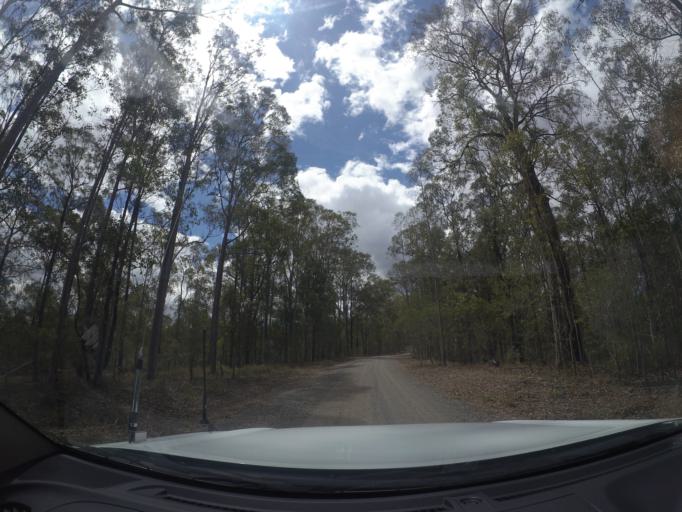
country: AU
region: Queensland
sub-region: Logan
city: Cedar Vale
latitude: -27.9071
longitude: 153.0306
